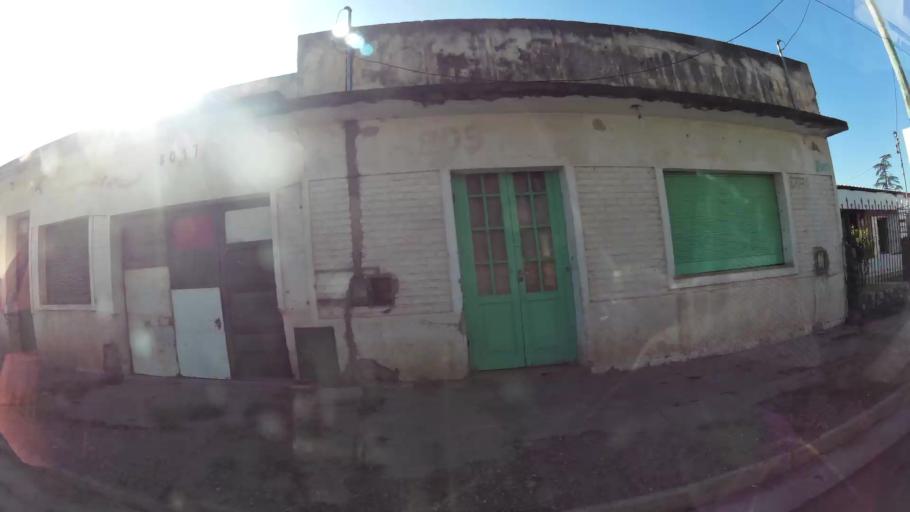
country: AR
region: Cordoba
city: Villa Allende
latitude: -31.3300
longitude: -64.2611
